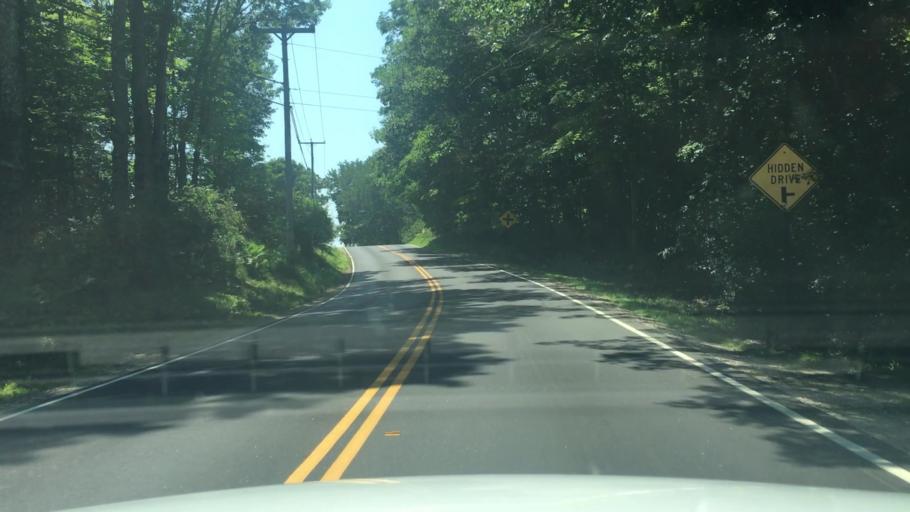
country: US
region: Maine
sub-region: Cumberland County
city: Cumberland Center
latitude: 43.7800
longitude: -70.2584
